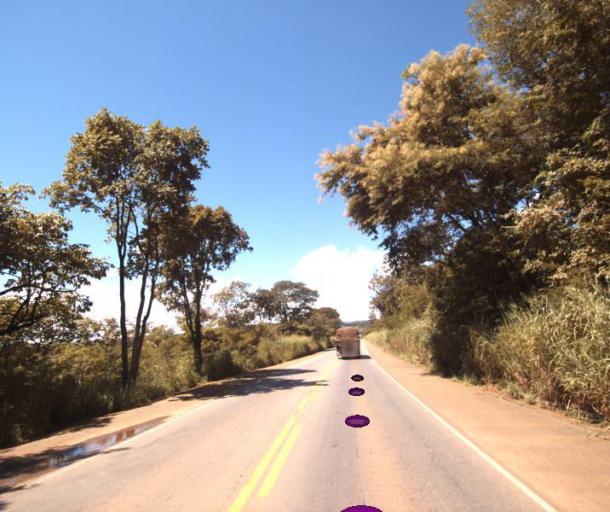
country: BR
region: Goias
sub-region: Pirenopolis
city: Pirenopolis
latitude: -16.0840
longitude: -49.0416
